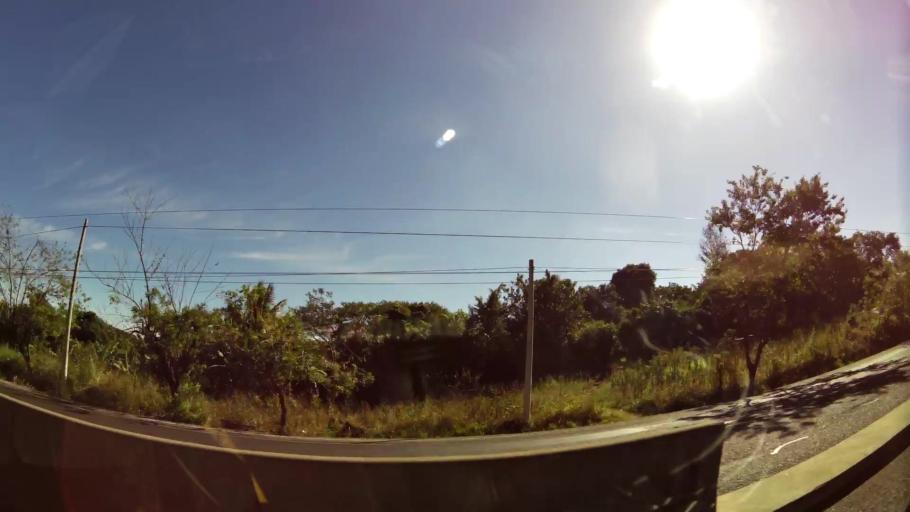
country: SV
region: Santa Ana
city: Coatepeque
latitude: 13.9158
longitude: -89.5170
